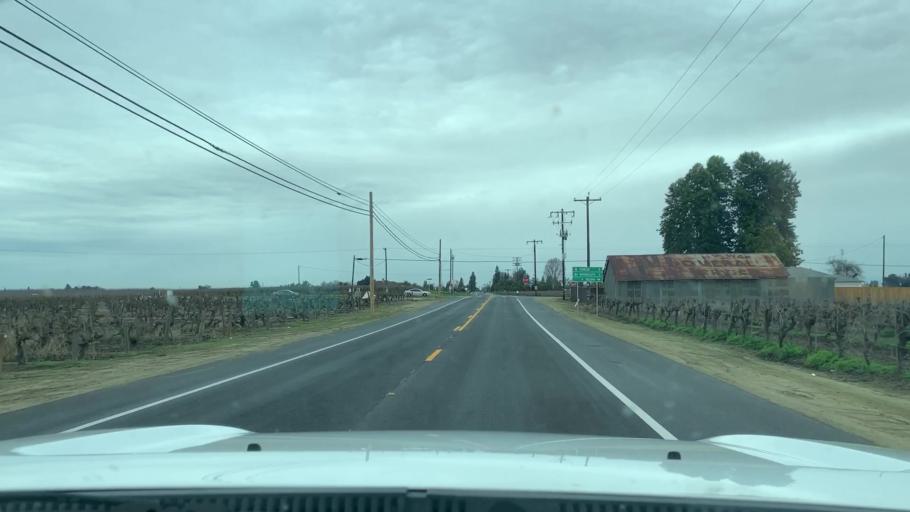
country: US
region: California
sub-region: Fresno County
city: Fowler
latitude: 36.5605
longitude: -119.6824
